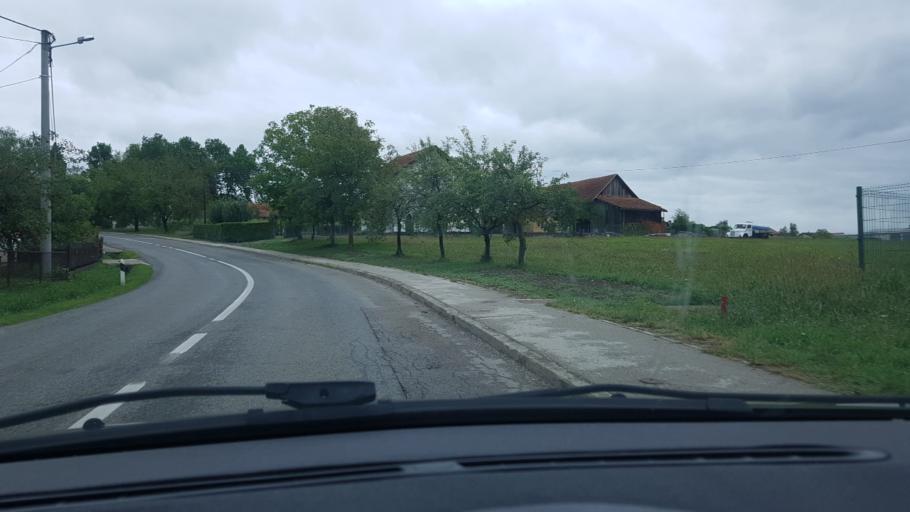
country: HR
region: Karlovacka
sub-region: Grad Karlovac
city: Karlovac
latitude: 45.5486
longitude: 15.5385
